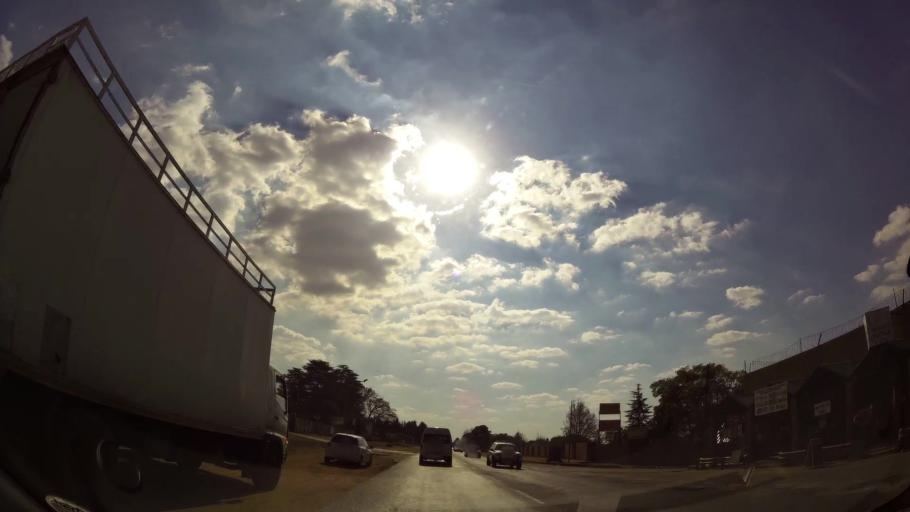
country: ZA
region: Gauteng
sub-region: Ekurhuleni Metropolitan Municipality
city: Benoni
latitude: -26.1272
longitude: 28.3553
